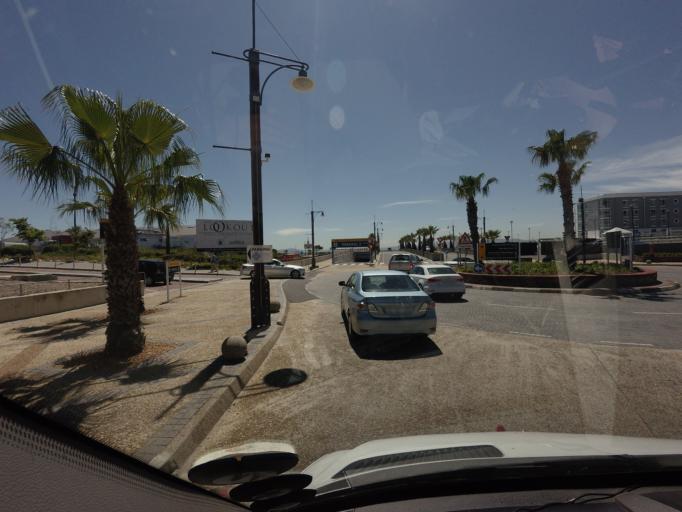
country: ZA
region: Western Cape
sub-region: City of Cape Town
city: Cape Town
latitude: -33.9033
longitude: 18.4164
